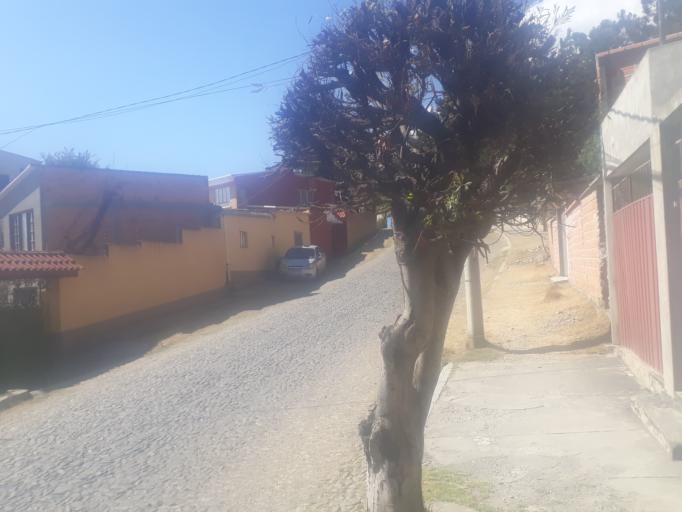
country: BO
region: La Paz
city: La Paz
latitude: -16.5384
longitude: -68.0562
